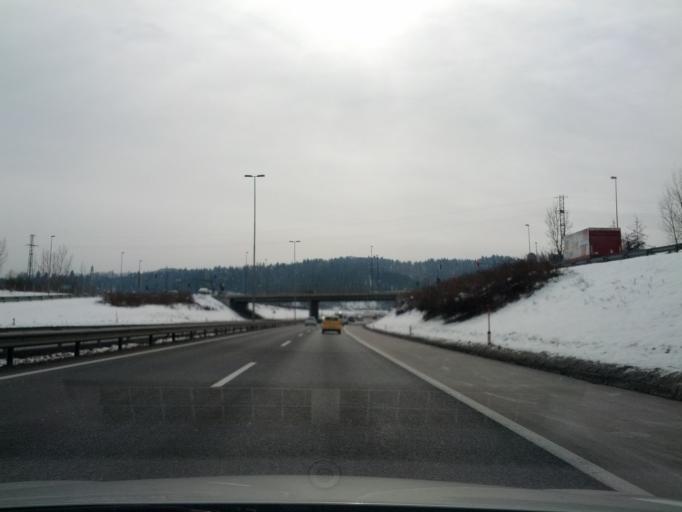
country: SI
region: Skofljica
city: Lavrica
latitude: 46.0454
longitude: 14.5763
